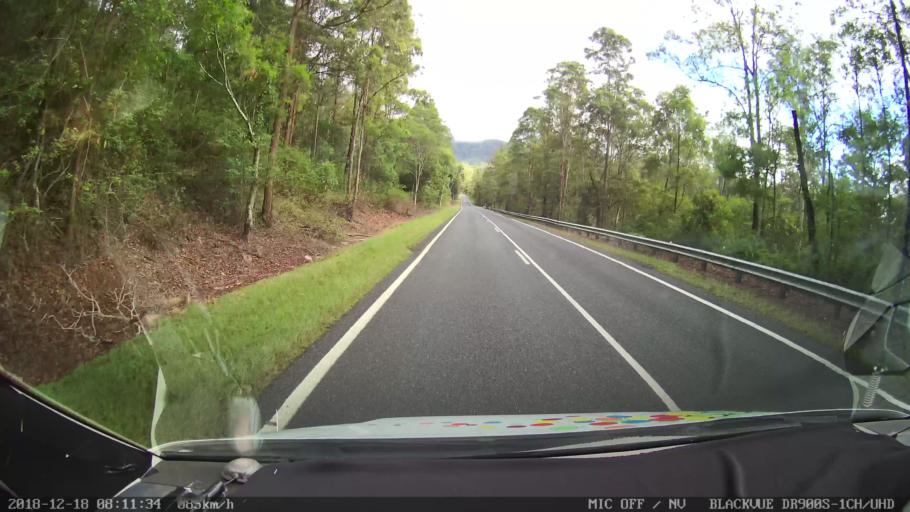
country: AU
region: New South Wales
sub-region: Kyogle
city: Kyogle
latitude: -28.3494
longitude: 152.6695
